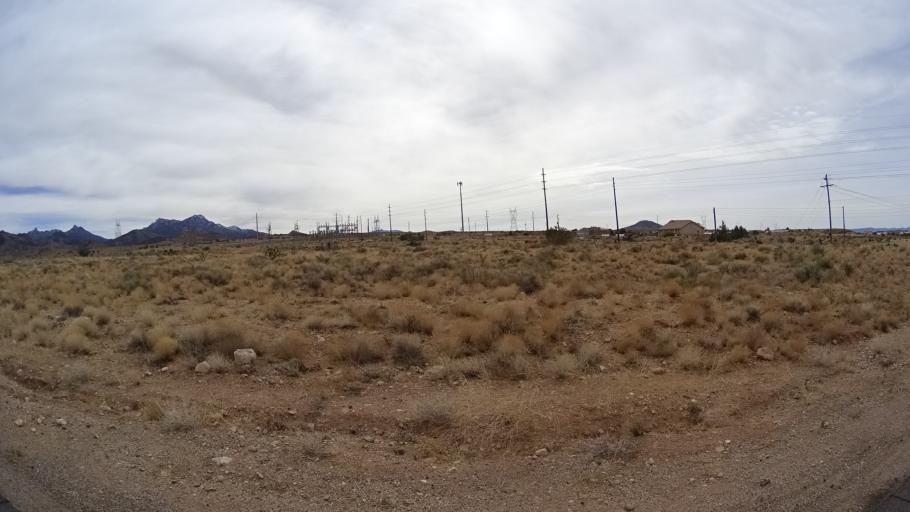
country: US
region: Arizona
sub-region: Mohave County
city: Kingman
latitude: 35.1813
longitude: -113.9819
